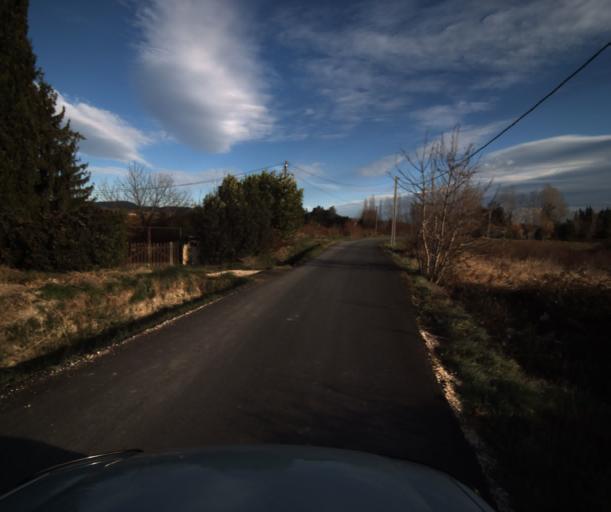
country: FR
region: Provence-Alpes-Cote d'Azur
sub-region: Departement du Vaucluse
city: Pertuis
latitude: 43.6744
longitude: 5.5055
